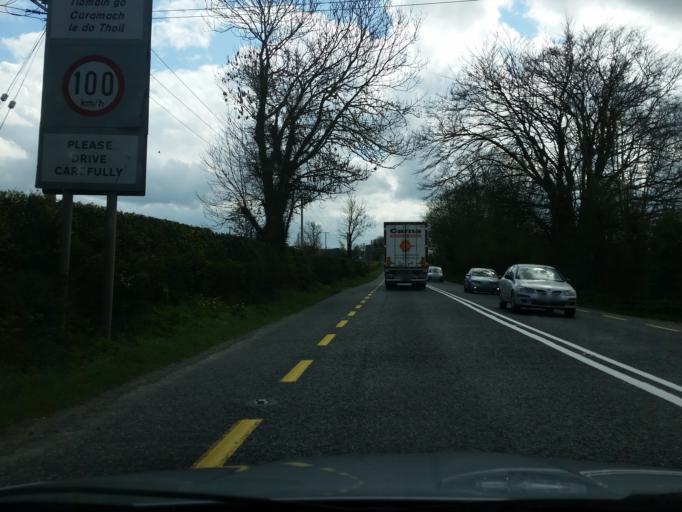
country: IE
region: Leinster
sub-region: An Mhi
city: Ratoath
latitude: 53.5570
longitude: -6.4392
